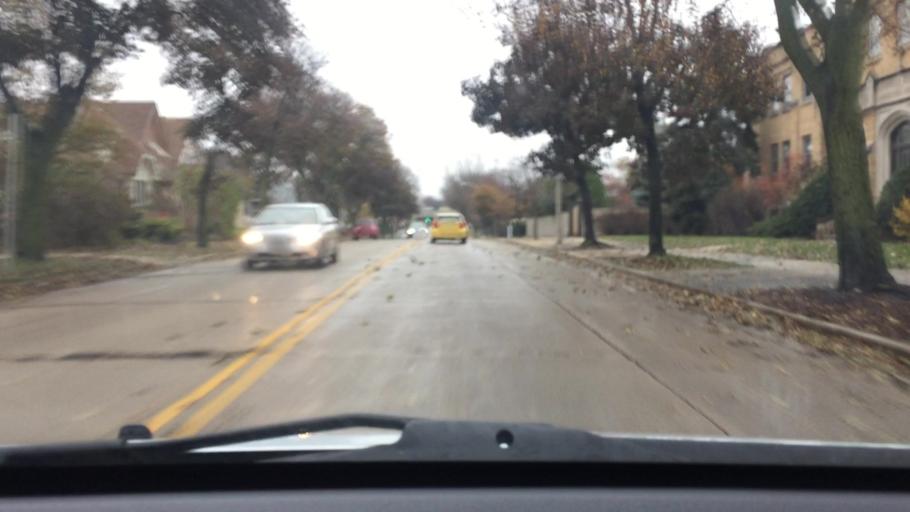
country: US
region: Wisconsin
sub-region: Milwaukee County
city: Wauwatosa
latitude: 43.0337
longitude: -87.9974
